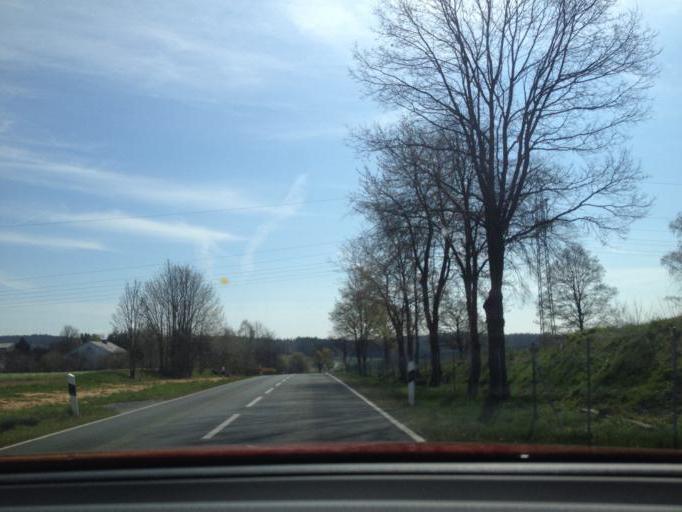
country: DE
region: Bavaria
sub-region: Upper Franconia
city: Roslau
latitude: 50.0788
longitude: 12.0081
